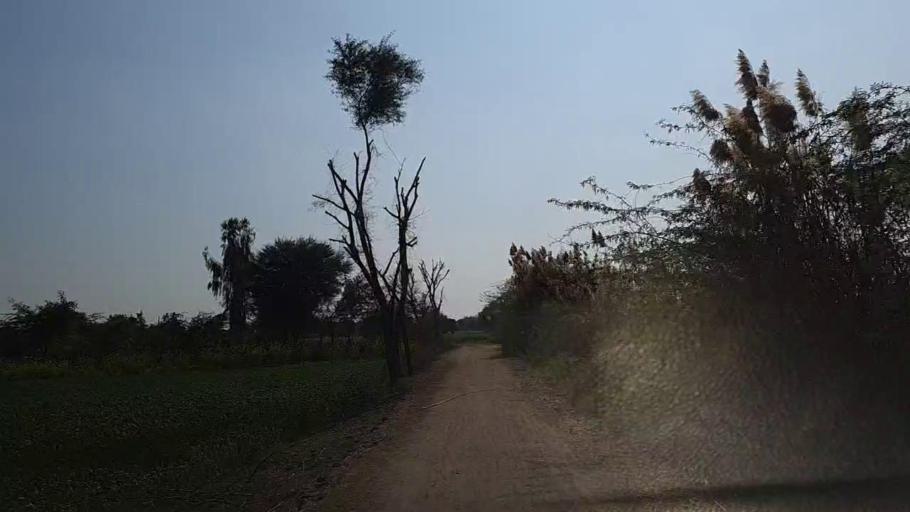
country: PK
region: Sindh
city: Jam Sahib
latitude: 26.2610
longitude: 68.5298
